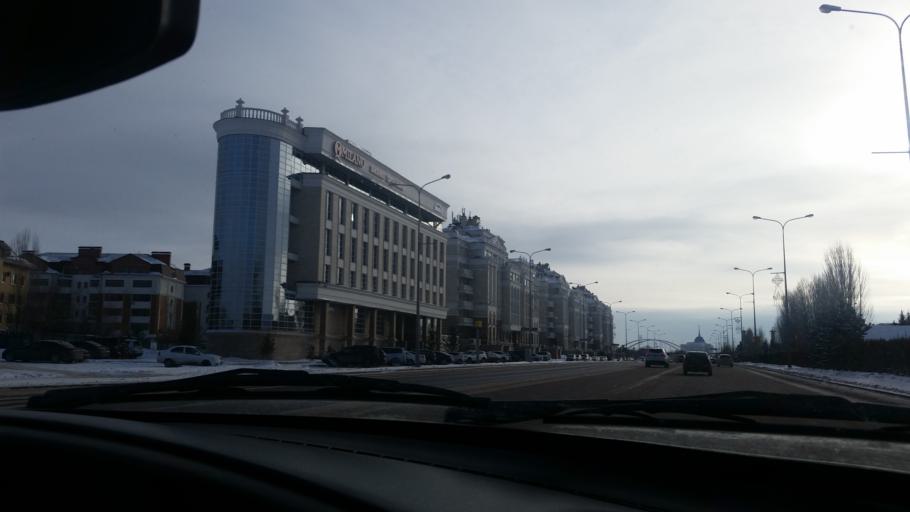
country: KZ
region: Astana Qalasy
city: Astana
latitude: 51.1456
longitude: 71.4448
